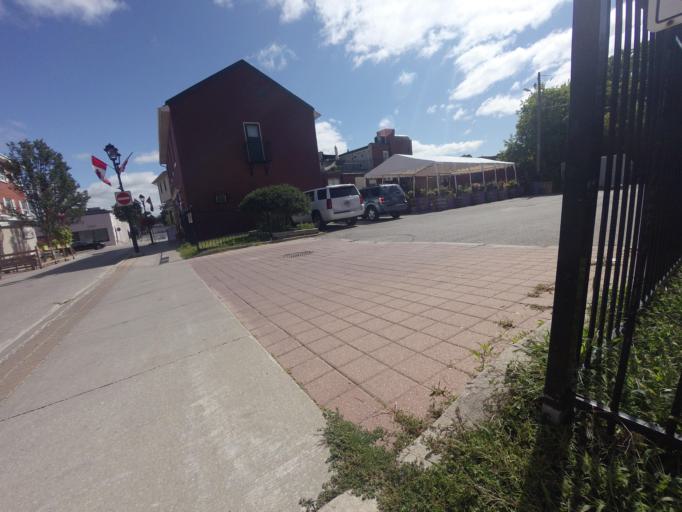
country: CA
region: Ontario
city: Newmarket
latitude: 44.0523
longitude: -79.4573
